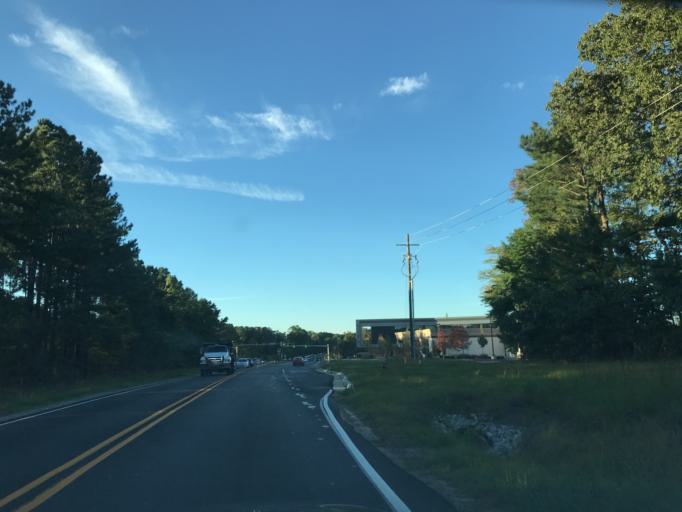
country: US
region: North Carolina
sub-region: Wake County
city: Morrisville
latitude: 35.8503
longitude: -78.8398
